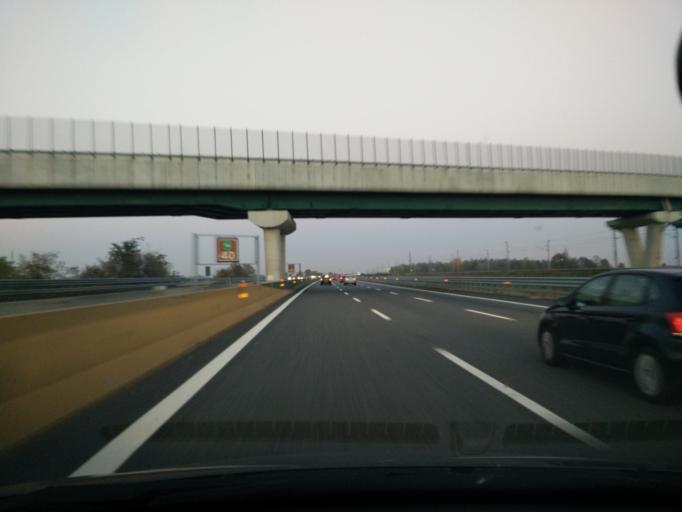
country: IT
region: Piedmont
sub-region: Provincia di Vercelli
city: Carisio
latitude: 45.4277
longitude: 8.1967
